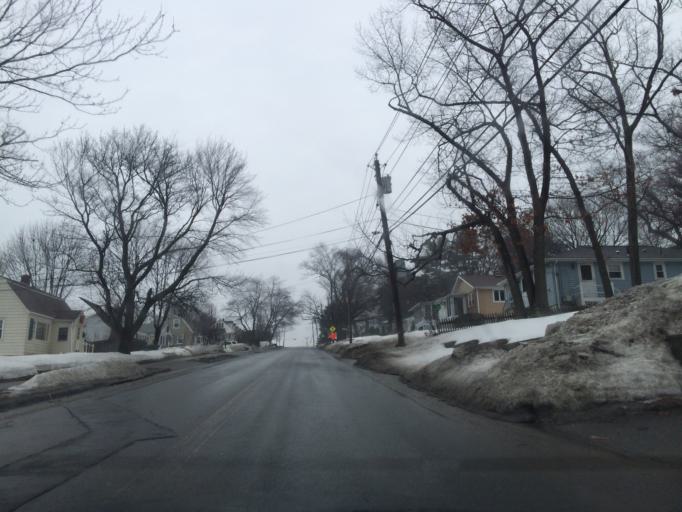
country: US
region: Massachusetts
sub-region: Middlesex County
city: Waltham
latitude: 42.4137
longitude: -71.2496
